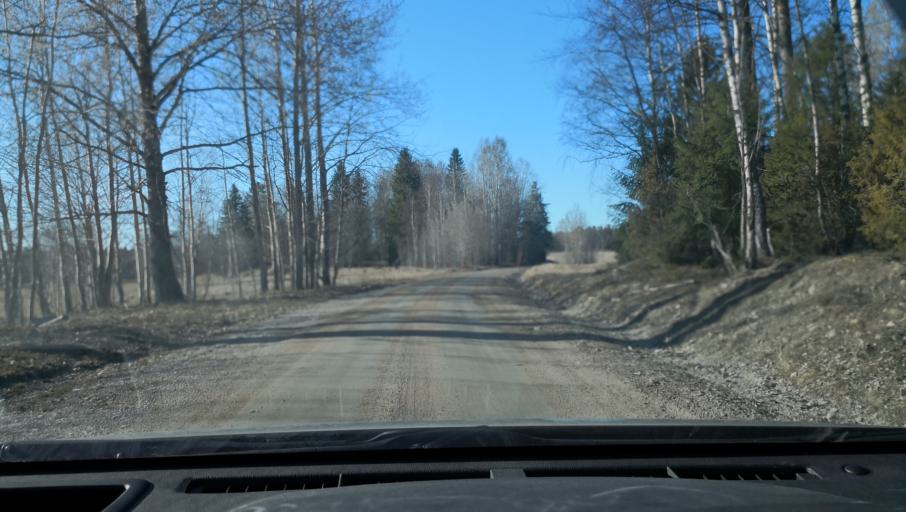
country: SE
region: Vaestmanland
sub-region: Sala Kommun
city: Sala
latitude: 60.1462
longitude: 16.6429
